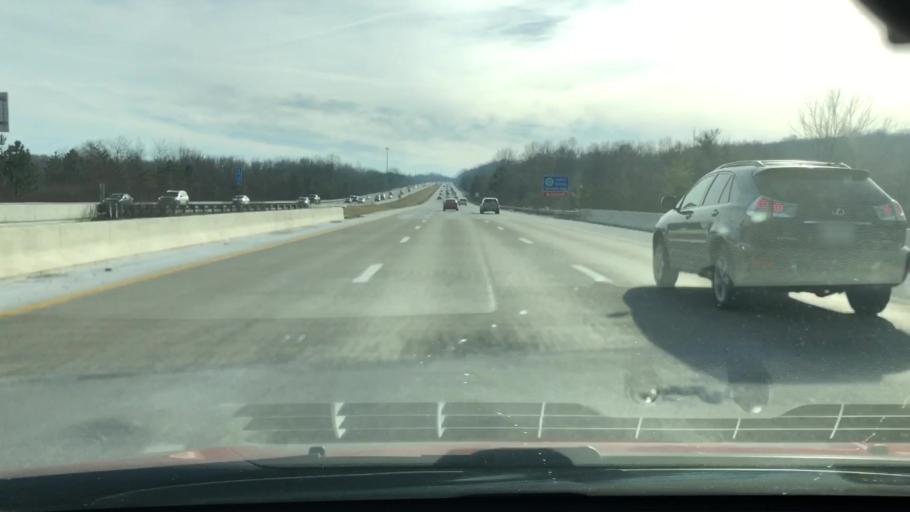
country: US
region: Ohio
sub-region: Greene County
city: Beavercreek
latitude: 39.7250
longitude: -84.0910
